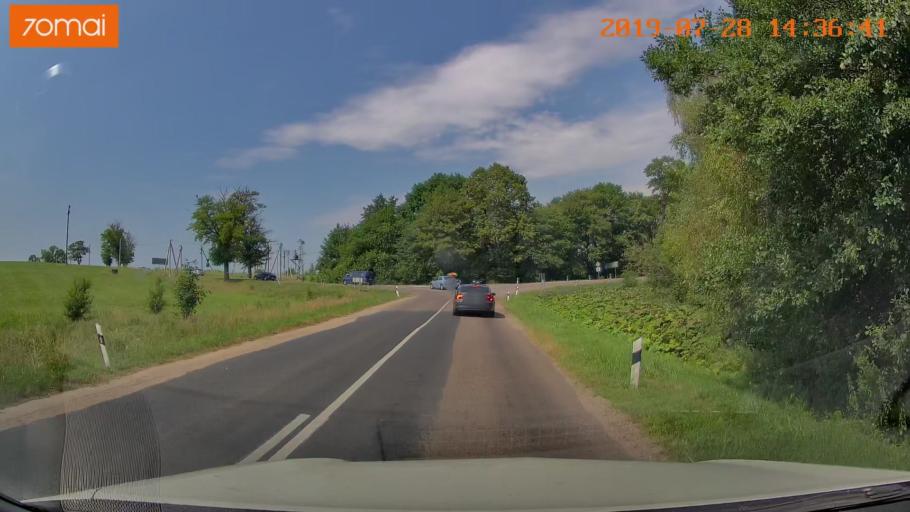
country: RU
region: Kaliningrad
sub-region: Gorod Kaliningrad
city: Yantarnyy
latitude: 54.8393
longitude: 20.0062
